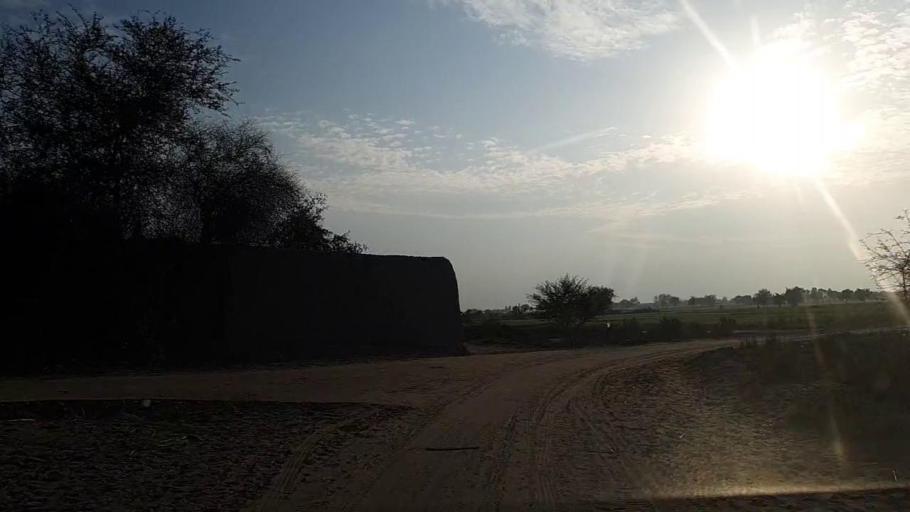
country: PK
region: Sindh
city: Jam Sahib
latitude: 26.3947
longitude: 68.5155
